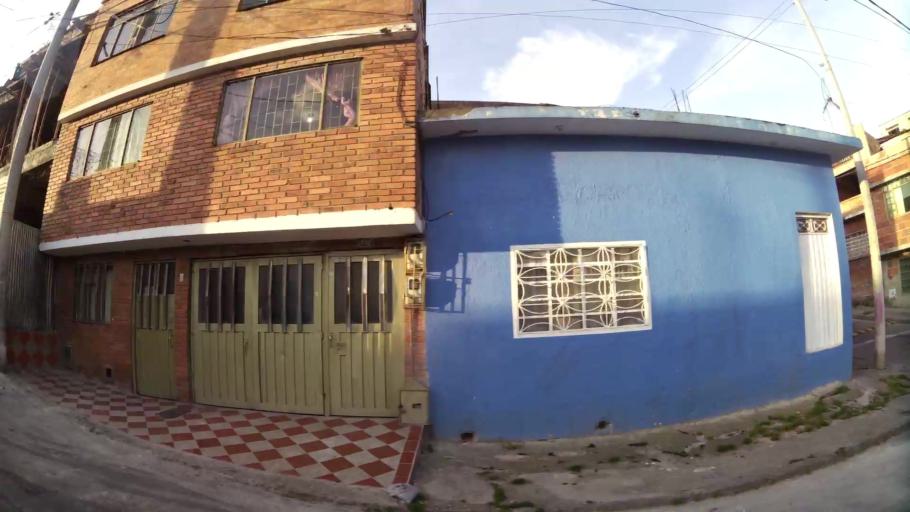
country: CO
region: Bogota D.C.
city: Bogota
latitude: 4.5426
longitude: -74.0863
